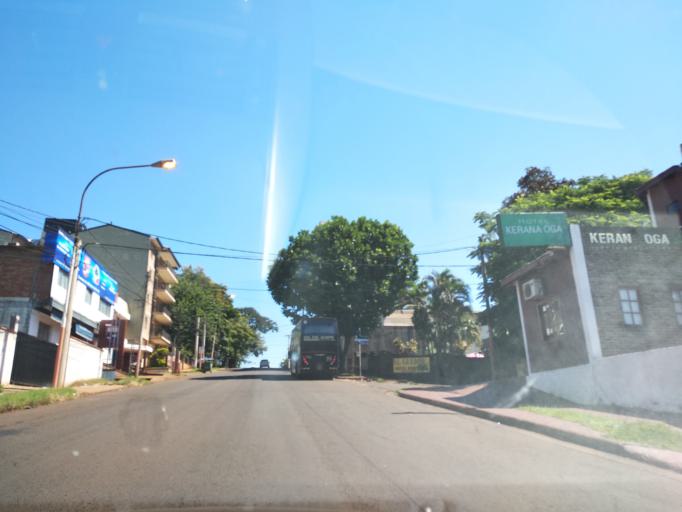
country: AR
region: Misiones
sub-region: Departamento de Iguazu
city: Puerto Iguazu
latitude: -25.5981
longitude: -54.5675
